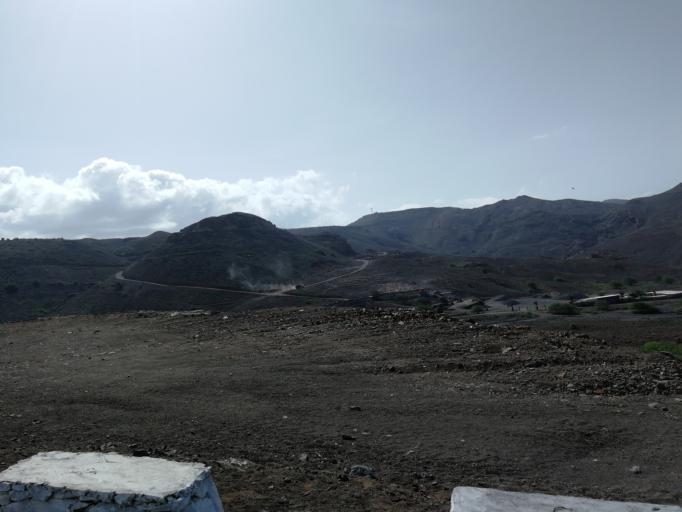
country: CV
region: Sao Vicente
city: Mindelo
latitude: 16.8829
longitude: -24.9401
